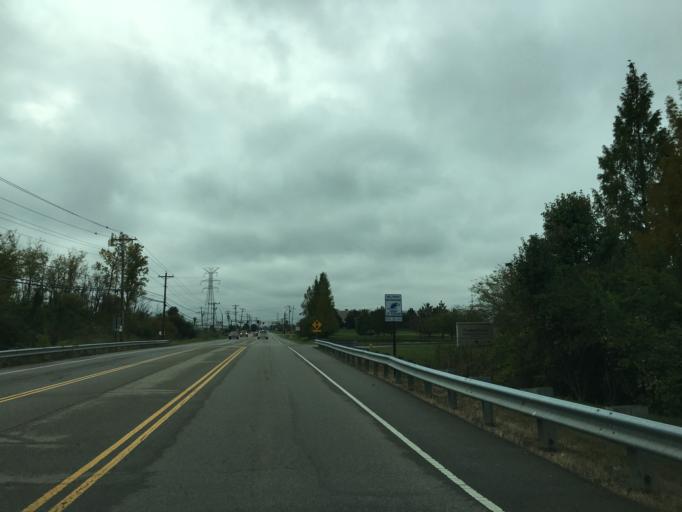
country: US
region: Ohio
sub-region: Butler County
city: Beckett Ridge
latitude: 39.3413
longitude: -84.4437
